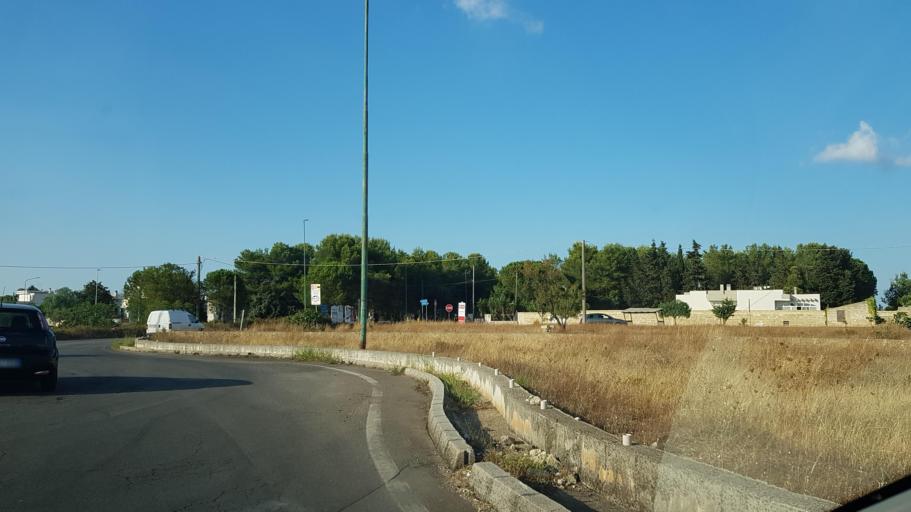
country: IT
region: Apulia
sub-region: Provincia di Lecce
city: Montesano Salentino
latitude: 39.9729
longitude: 18.3263
